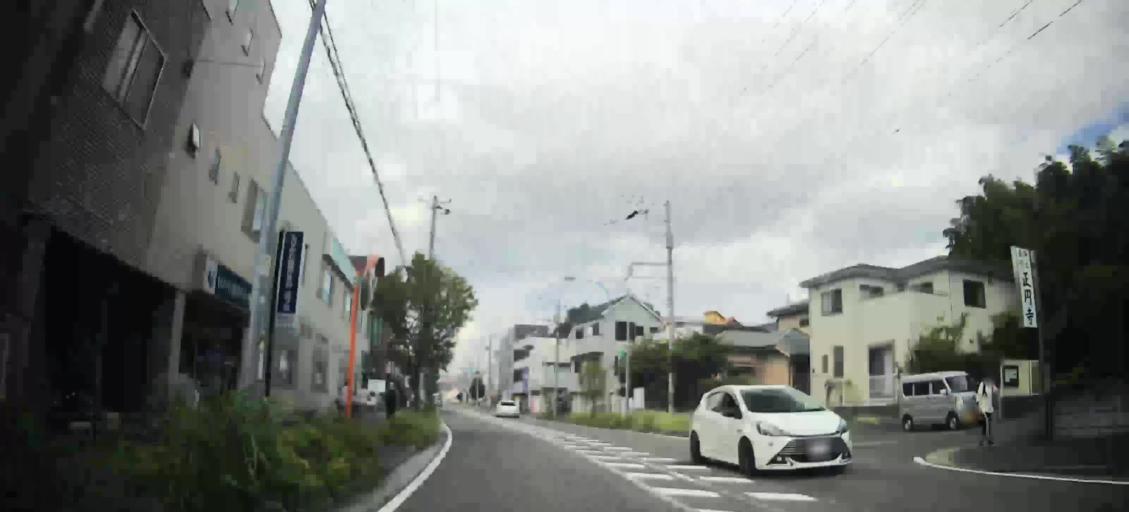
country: JP
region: Kanagawa
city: Minami-rinkan
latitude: 35.4865
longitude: 139.5438
